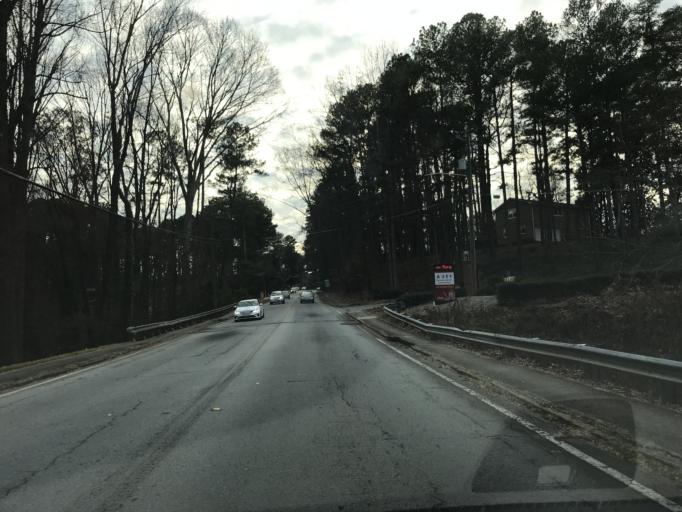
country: US
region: Georgia
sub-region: DeKalb County
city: Tucker
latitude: 33.8593
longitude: -84.2534
